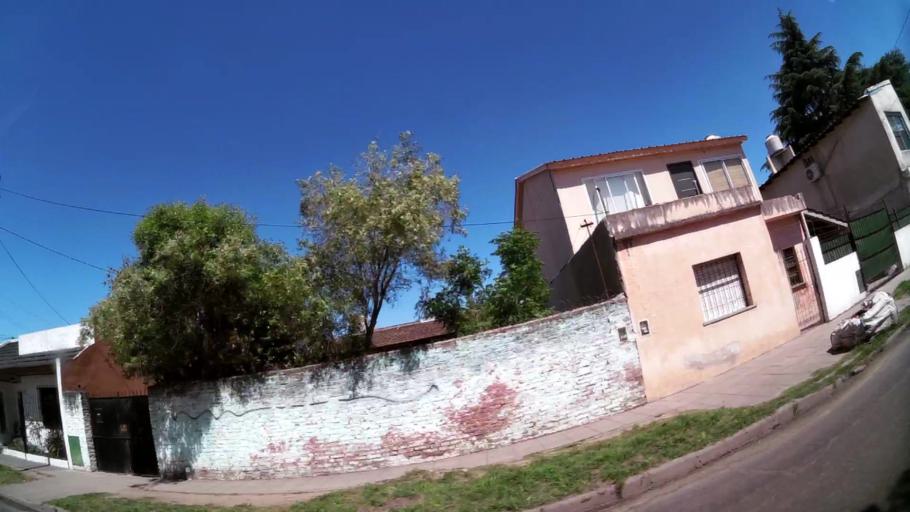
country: AR
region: Buenos Aires
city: Hurlingham
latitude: -34.5082
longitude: -58.6724
